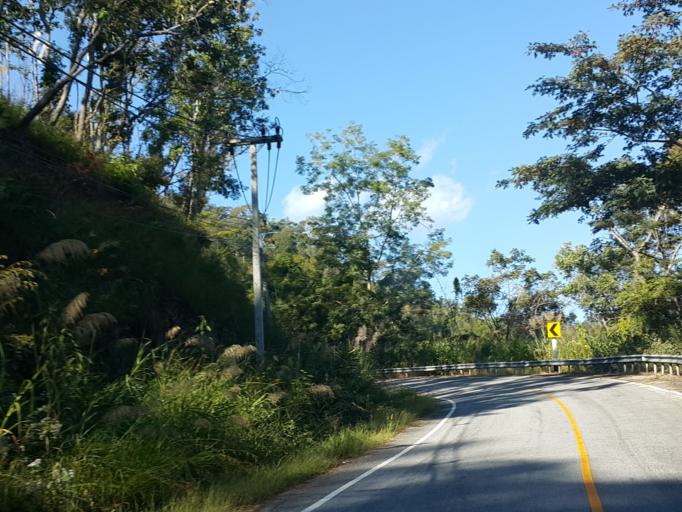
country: TH
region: Chiang Mai
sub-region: Amphoe Chiang Dao
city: Chiang Dao
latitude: 19.5274
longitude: 98.8813
